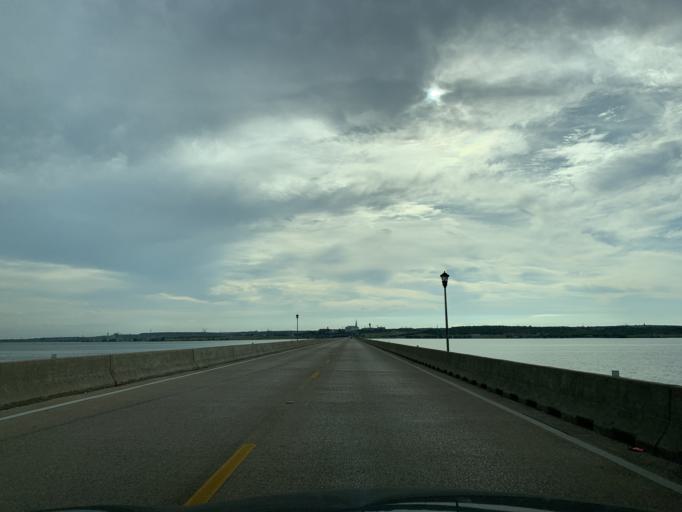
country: US
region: Texas
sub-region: Dallas County
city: Grand Prairie
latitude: 32.7062
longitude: -96.9743
